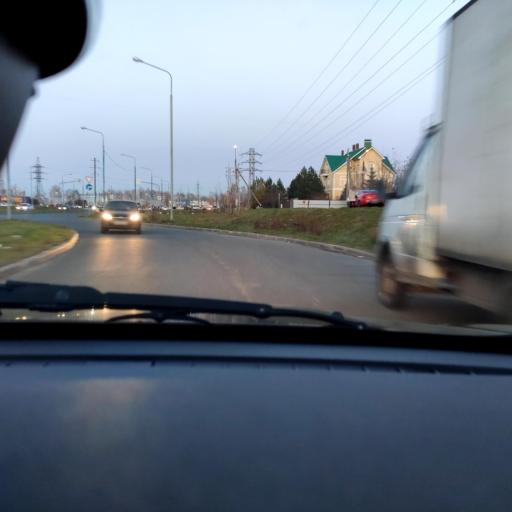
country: RU
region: Samara
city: Tol'yatti
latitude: 53.5439
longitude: 49.3706
